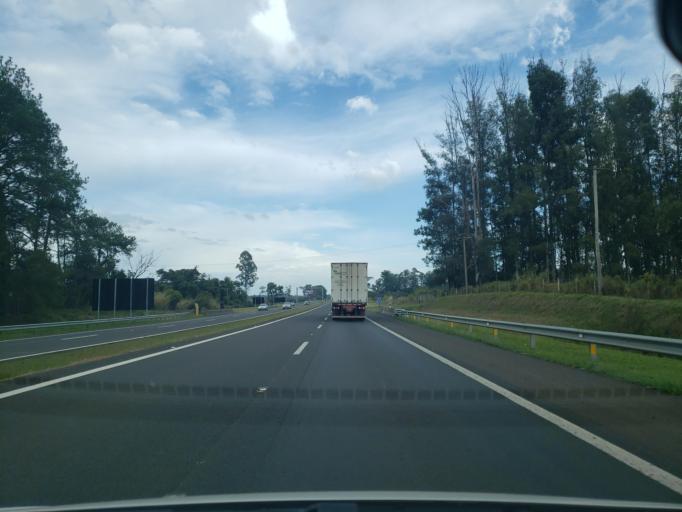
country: BR
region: Sao Paulo
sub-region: Itirapina
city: Itirapina
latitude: -22.2648
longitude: -47.9120
